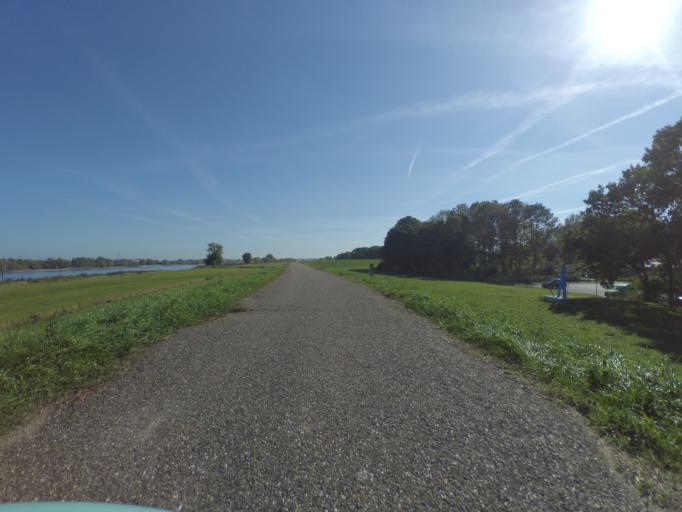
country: NL
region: Gelderland
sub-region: Gemeente Zevenaar
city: Zevenaar
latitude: 51.8650
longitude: 6.0550
